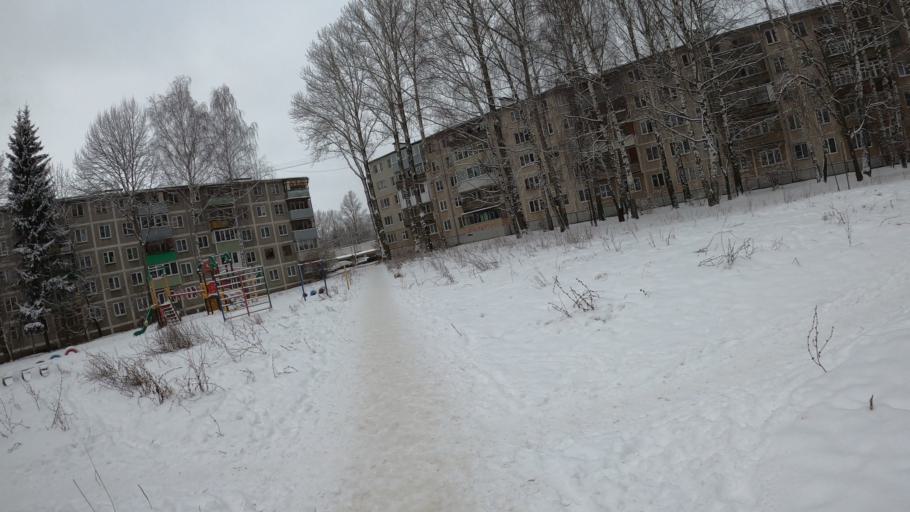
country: RU
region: Jaroslavl
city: Pereslavl'-Zalesskiy
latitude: 56.7518
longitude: 38.8721
